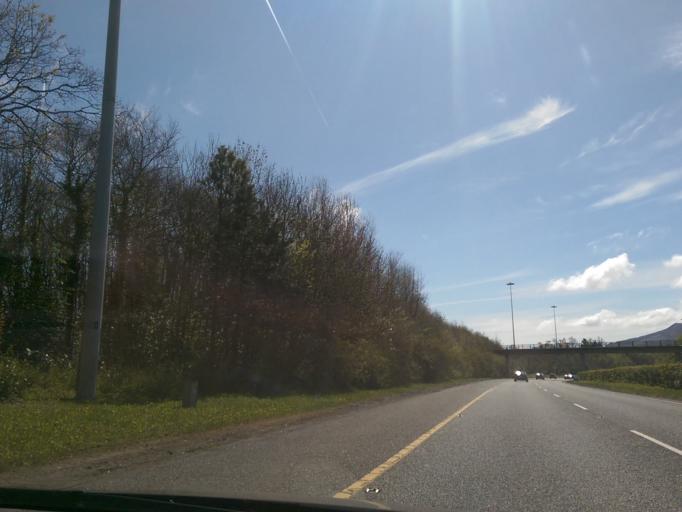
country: IE
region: Leinster
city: Little Bray
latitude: 53.2144
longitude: -6.1253
